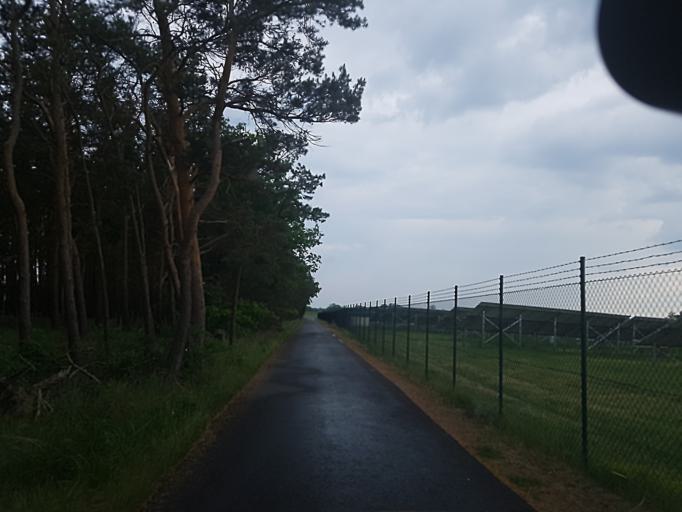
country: DE
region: Saxony-Anhalt
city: Elster
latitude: 51.8174
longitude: 12.8652
